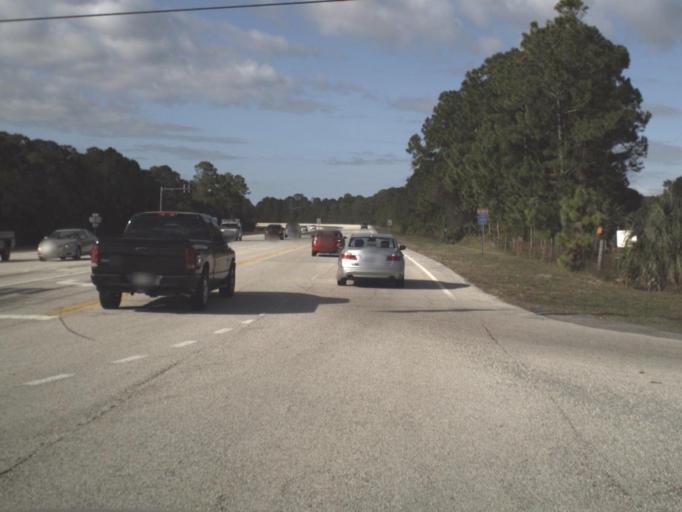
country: US
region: Florida
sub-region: Volusia County
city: South Daytona
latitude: 29.1592
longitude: -81.0671
